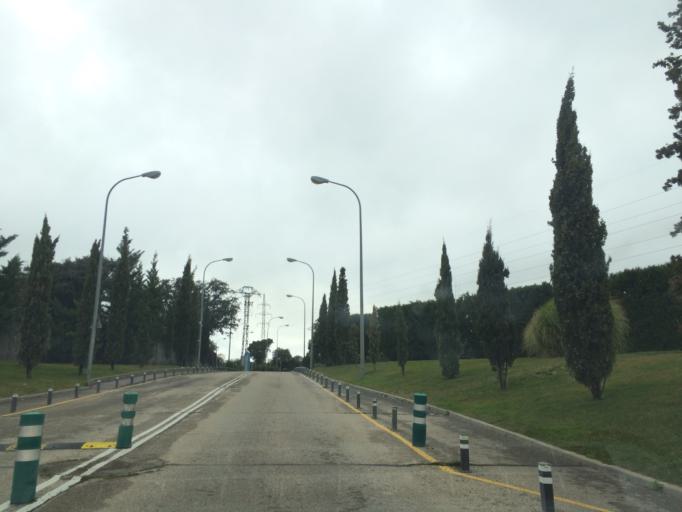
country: ES
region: Madrid
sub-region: Provincia de Madrid
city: Tres Cantos
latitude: 40.5781
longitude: -3.6995
